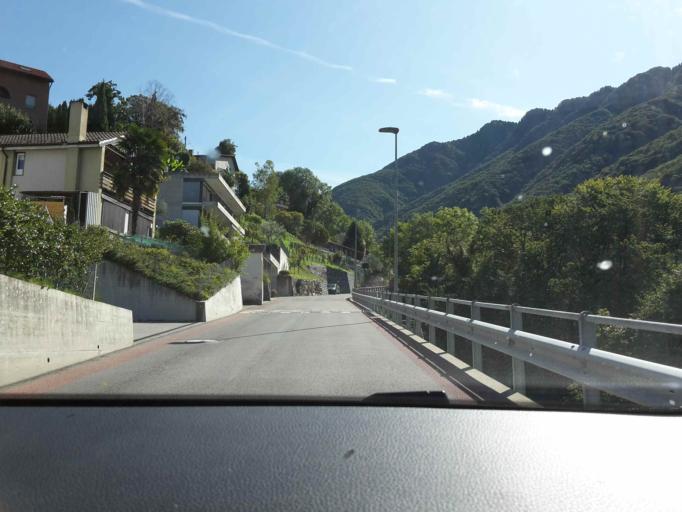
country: CH
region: Ticino
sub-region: Bellinzona District
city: Giubiasco
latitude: 46.1694
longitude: 9.0253
